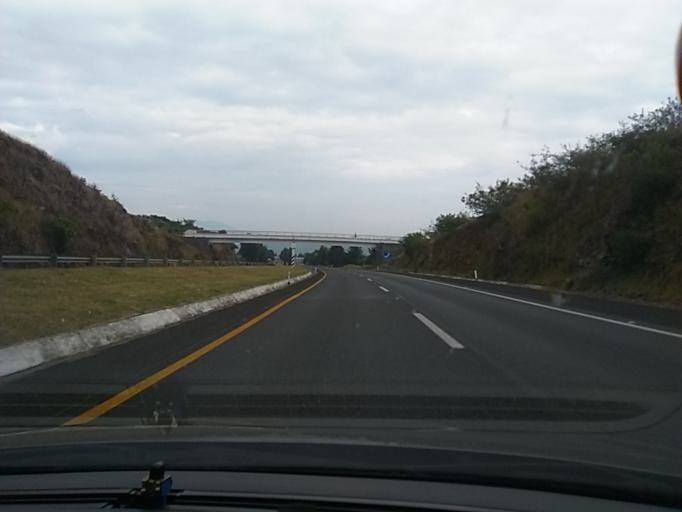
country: MX
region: Michoacan
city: Panindicuaro de la Reforma
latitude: 19.9962
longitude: -101.8604
